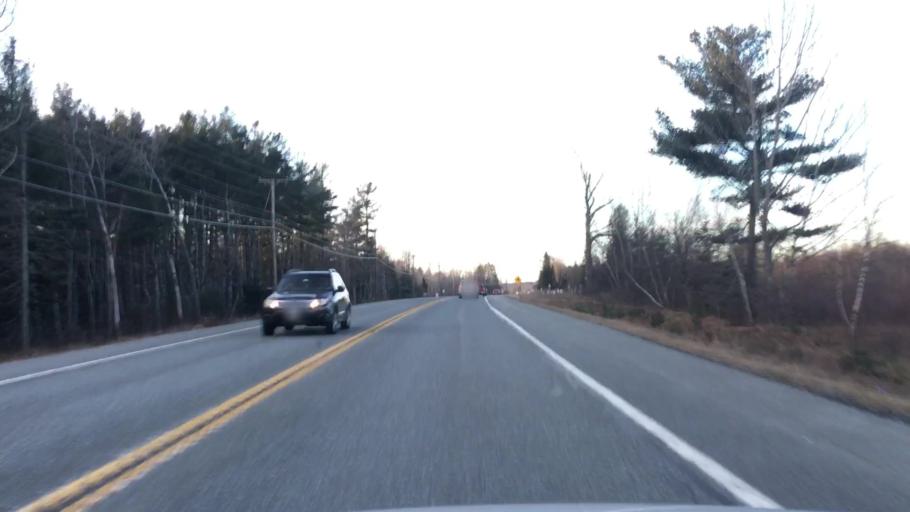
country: US
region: Maine
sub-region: Hancock County
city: Surry
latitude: 44.6188
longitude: -68.5283
